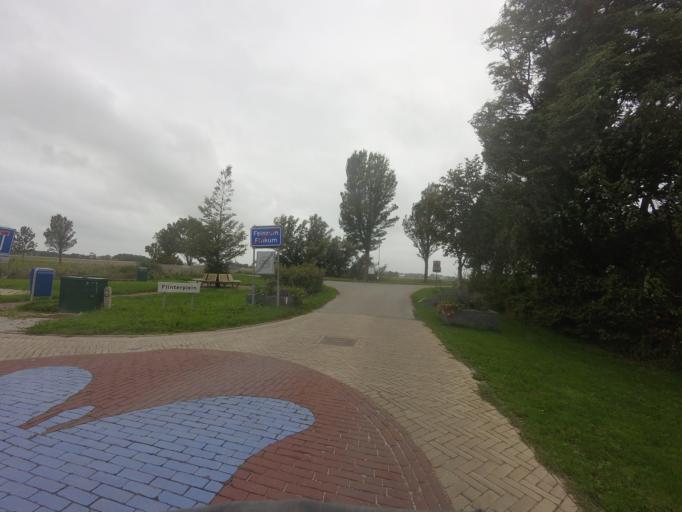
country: NL
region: Friesland
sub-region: Gemeente Leeuwarderadeel
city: Stiens
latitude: 53.2798
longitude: 5.7508
